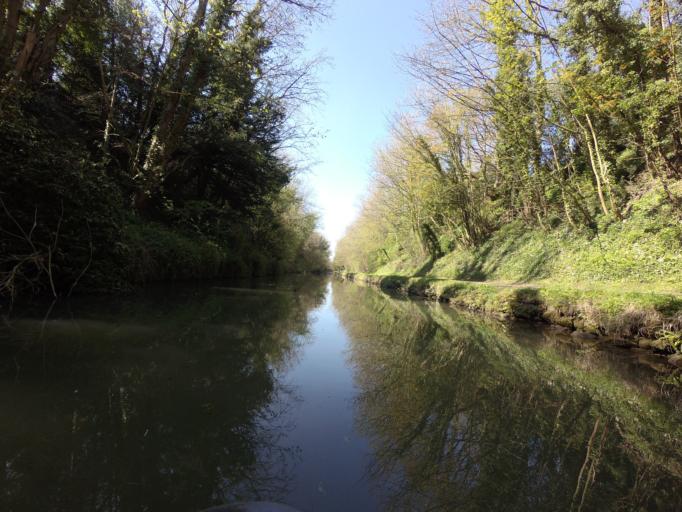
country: GB
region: England
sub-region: Hertfordshire
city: Tring
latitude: 51.8040
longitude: -0.6363
